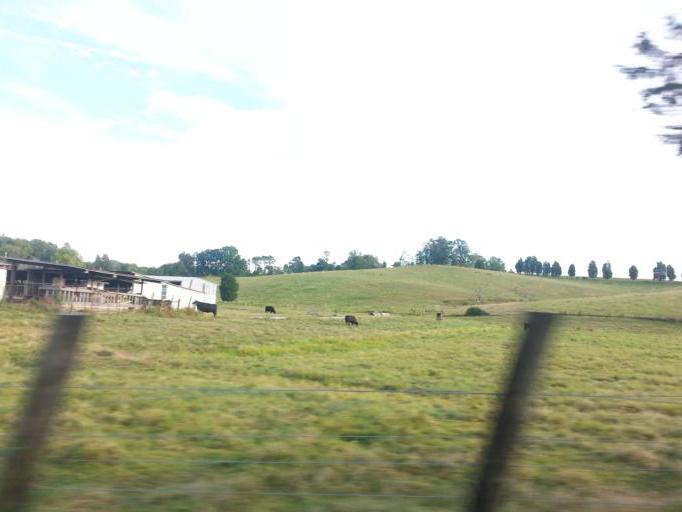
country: US
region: Tennessee
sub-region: Blount County
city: Wildwood
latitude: 35.8190
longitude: -83.8951
